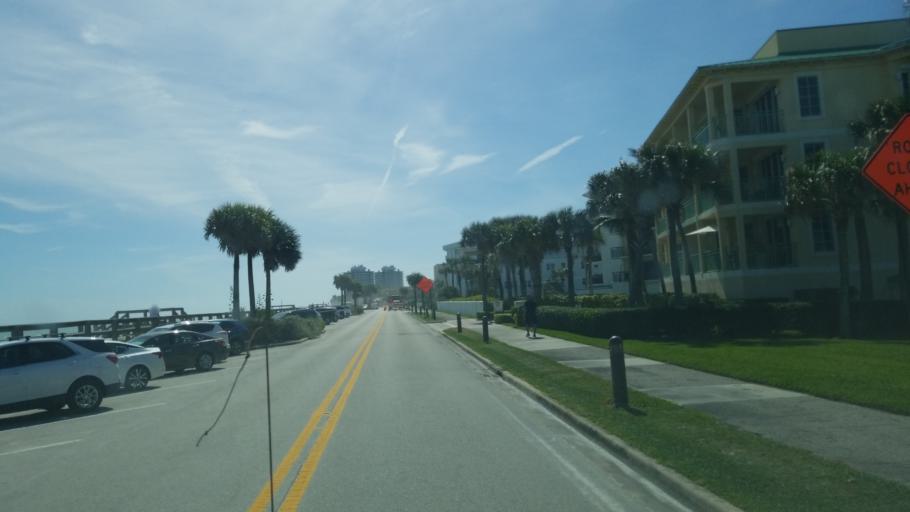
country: US
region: Florida
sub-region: Indian River County
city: Vero Beach
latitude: 27.6635
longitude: -80.3587
